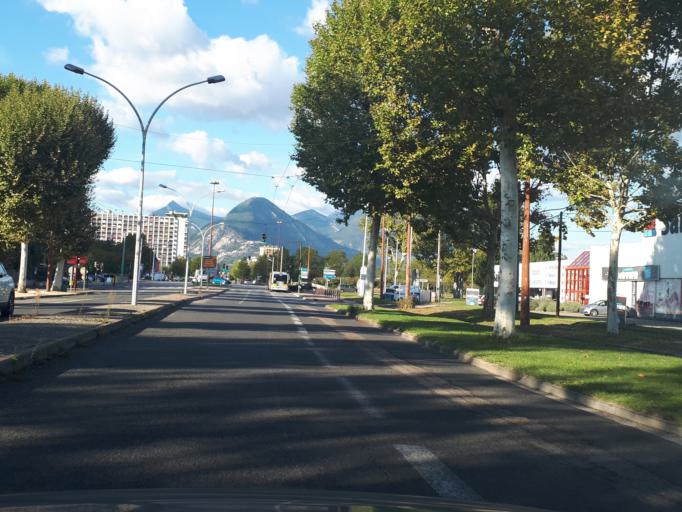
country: FR
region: Rhone-Alpes
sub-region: Departement de l'Isere
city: Grenoble
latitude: 45.1571
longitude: 5.7087
